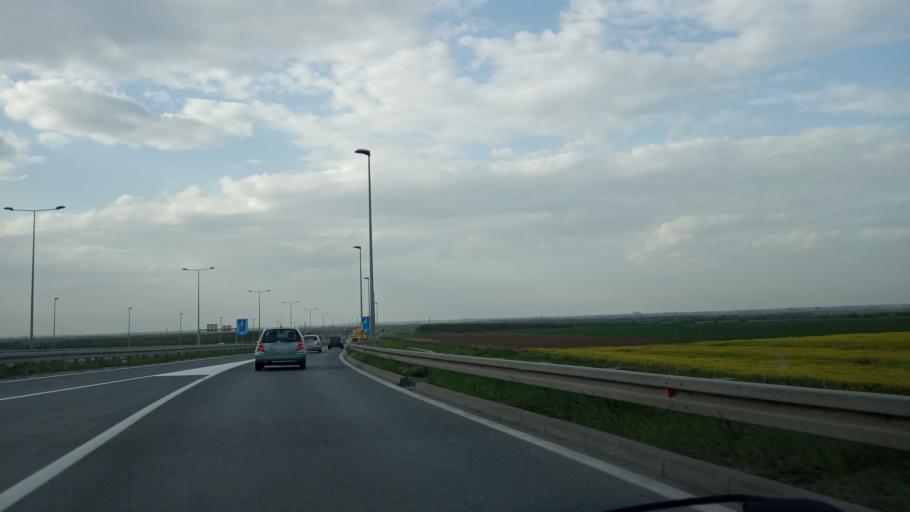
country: RS
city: Dobanovci
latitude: 44.8380
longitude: 20.2509
